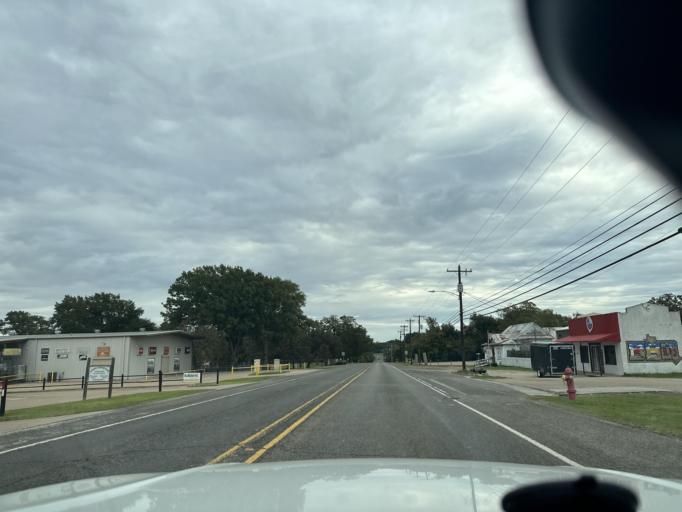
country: US
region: Texas
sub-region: Washington County
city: Brenham
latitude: 30.1656
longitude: -96.4175
